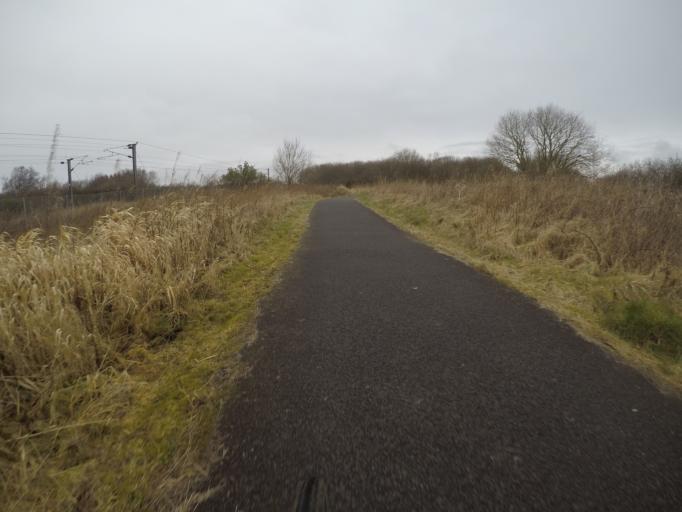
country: GB
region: Scotland
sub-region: North Ayrshire
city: Kilwinning
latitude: 55.6317
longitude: -4.6911
